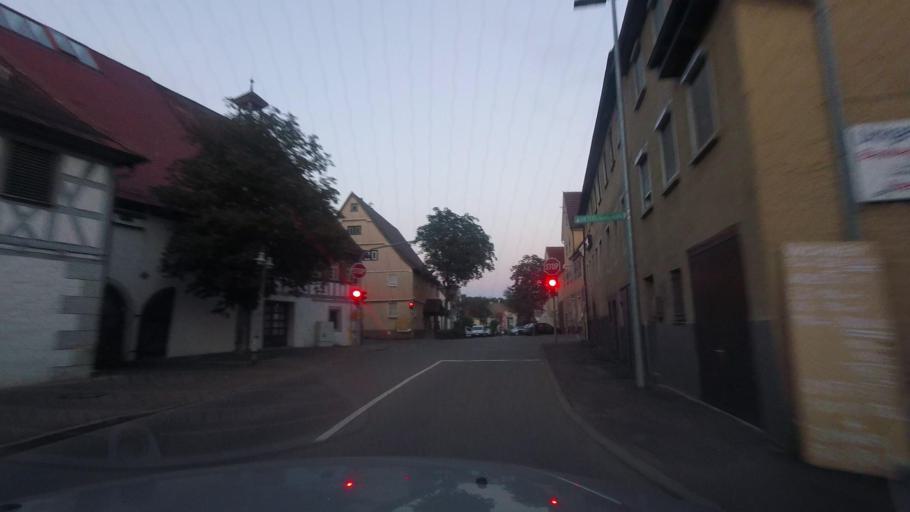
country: DE
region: Baden-Wuerttemberg
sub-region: Regierungsbezirk Stuttgart
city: Benningen am Neckar
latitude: 48.9478
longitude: 9.2420
